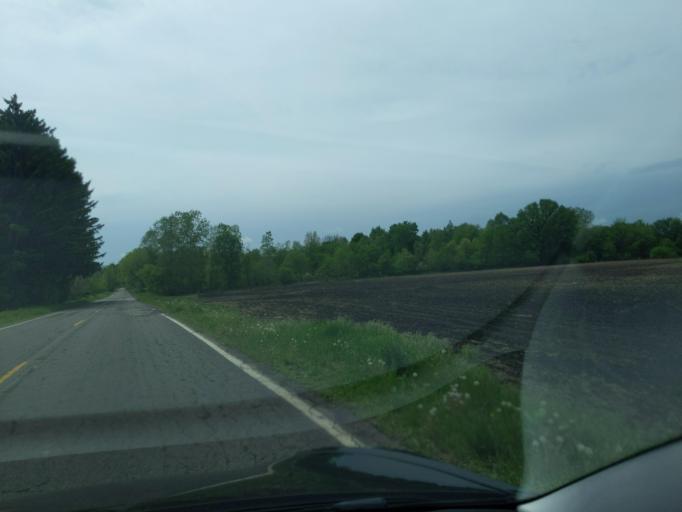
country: US
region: Michigan
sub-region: Ingham County
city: Stockbridge
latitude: 42.4247
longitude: -84.2489
